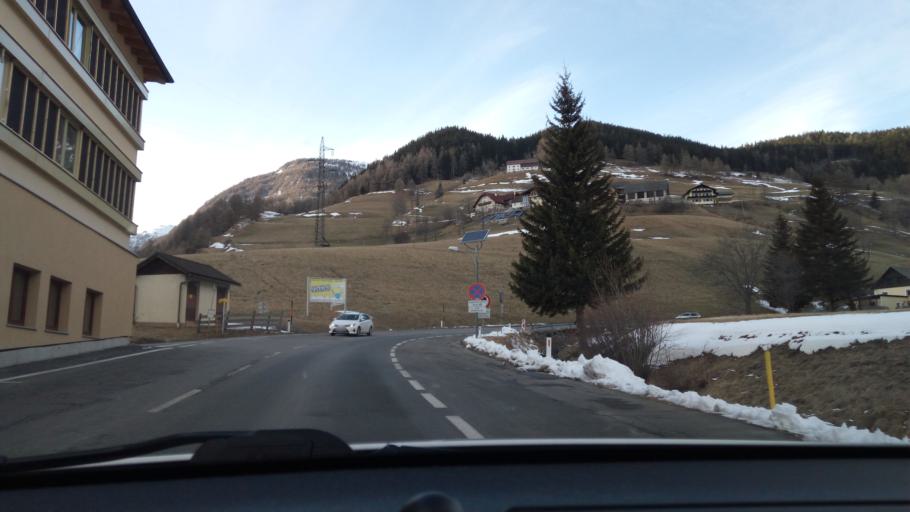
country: AT
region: Salzburg
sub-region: Politischer Bezirk Tamsweg
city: Sankt Michael im Lungau
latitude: 47.0306
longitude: 13.6035
